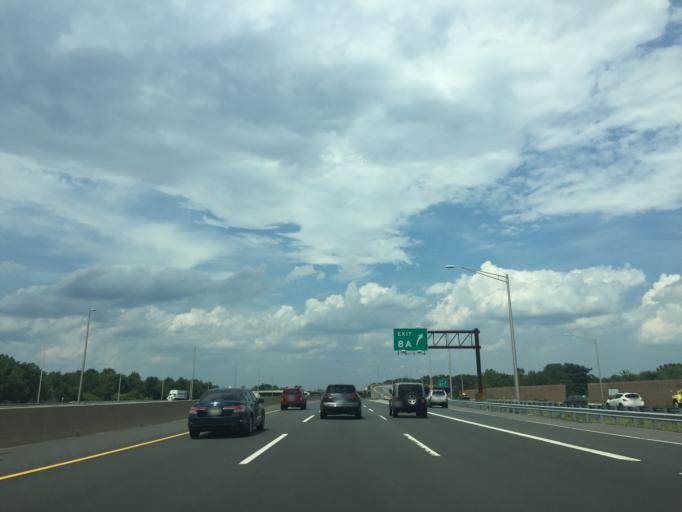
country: US
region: New Jersey
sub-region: Middlesex County
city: Rossmoor
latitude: 40.3460
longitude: -74.4755
